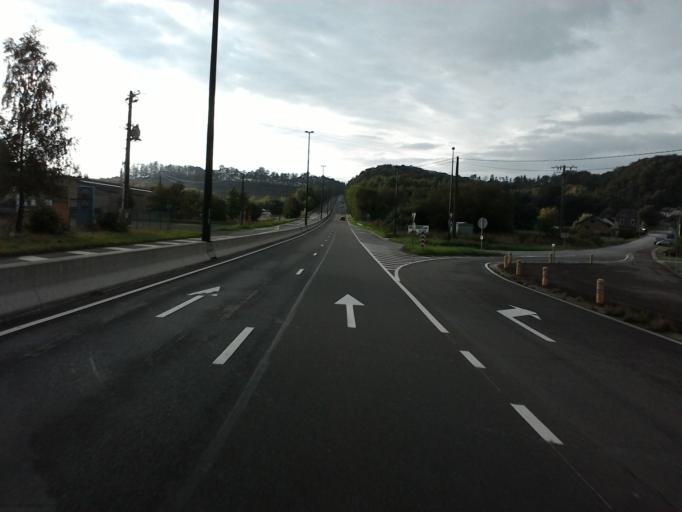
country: BE
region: Wallonia
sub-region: Province du Luxembourg
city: Attert
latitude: 49.7242
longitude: 5.7973
